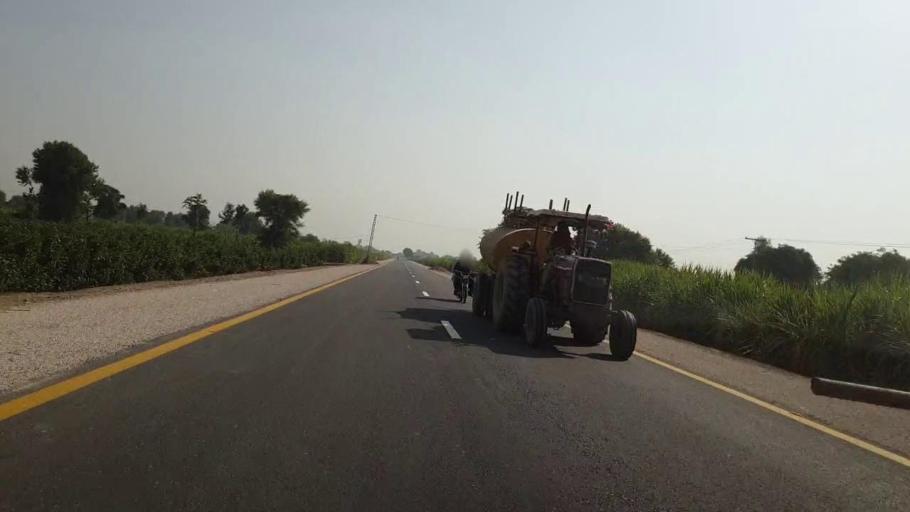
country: PK
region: Sindh
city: Bhan
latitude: 26.6113
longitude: 67.7786
